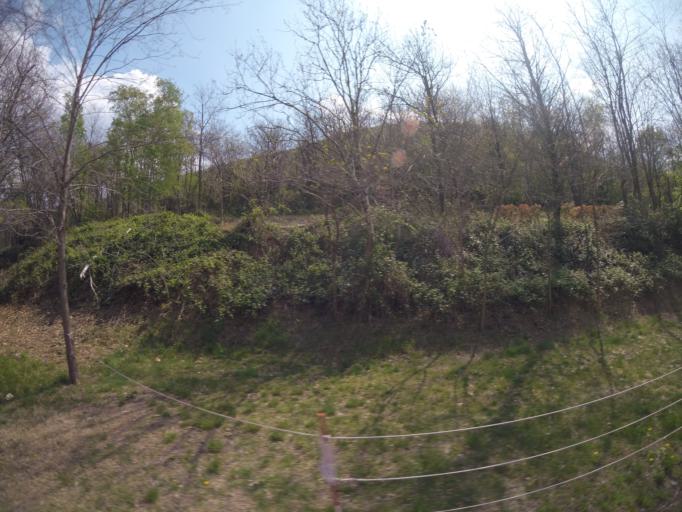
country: IT
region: Piedmont
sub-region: Provincia di Novara
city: Pettenasco
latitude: 45.8378
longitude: 8.3999
